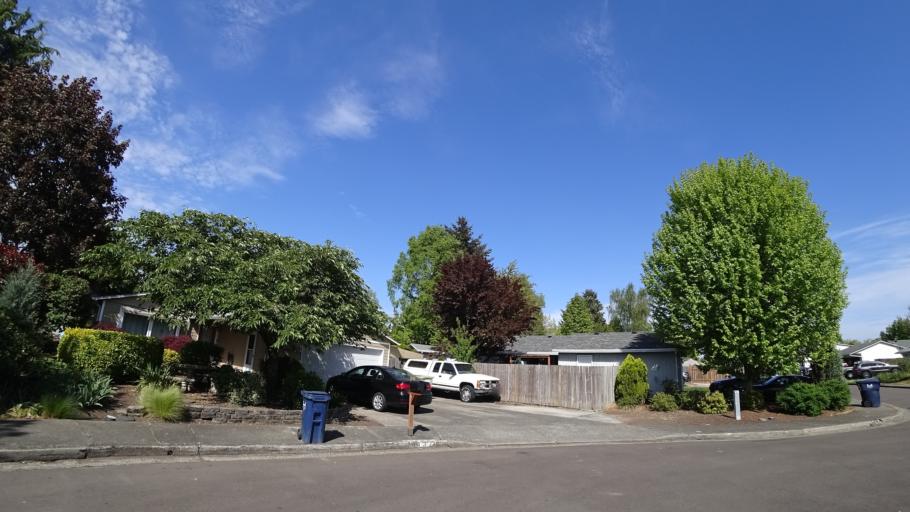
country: US
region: Oregon
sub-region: Washington County
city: Aloha
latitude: 45.4982
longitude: -122.8876
